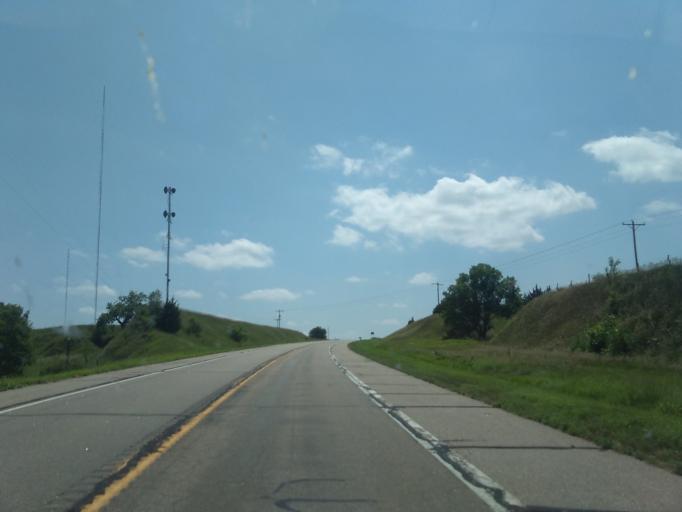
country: US
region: Nebraska
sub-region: Dawson County
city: Lexington
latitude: 40.7024
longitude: -99.7884
